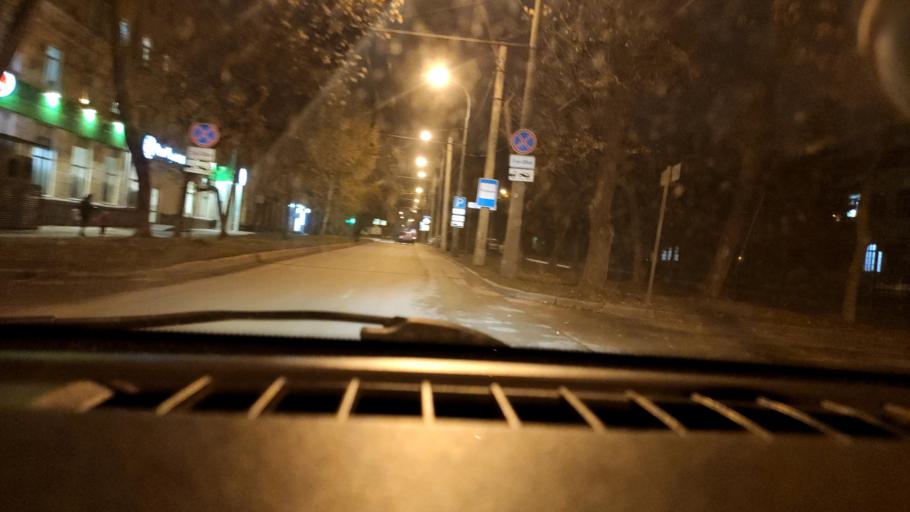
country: RU
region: Samara
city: Samara
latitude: 53.2170
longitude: 50.2518
